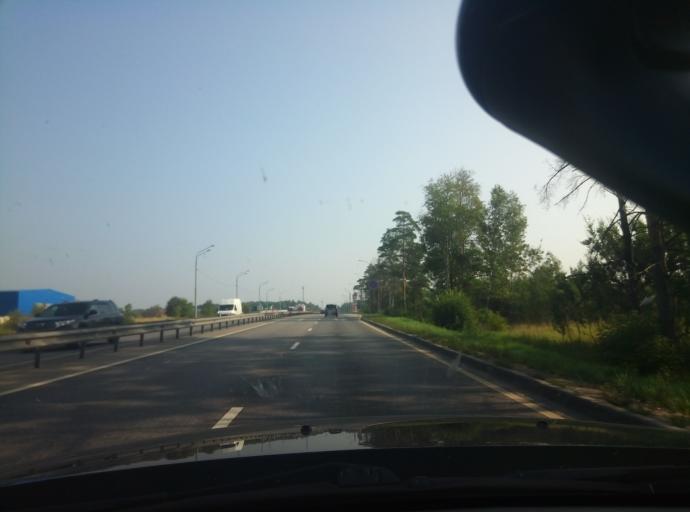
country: RU
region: Kaluga
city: Obninsk
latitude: 55.0722
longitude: 36.6261
